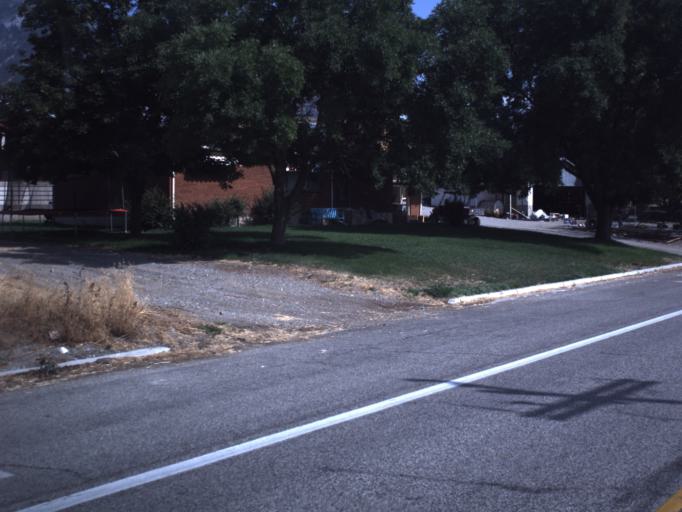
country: US
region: Utah
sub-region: Box Elder County
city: Honeyville
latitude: 41.6637
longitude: -112.0883
